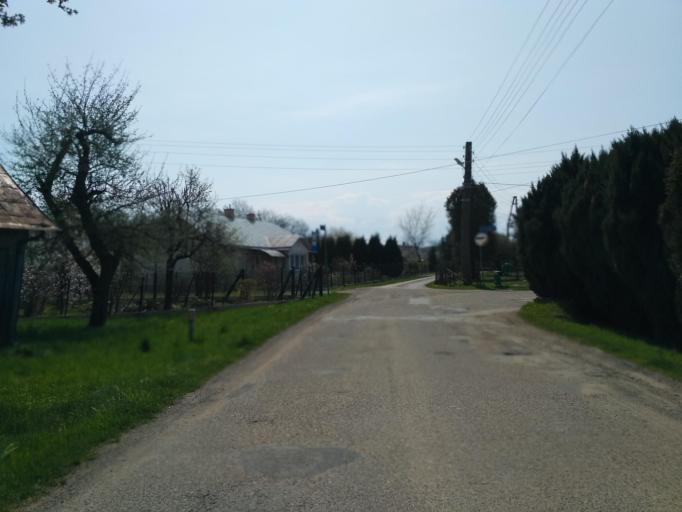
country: PL
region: Subcarpathian Voivodeship
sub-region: Powiat krosnienski
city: Miejsce Piastowe
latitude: 49.6240
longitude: 21.7313
